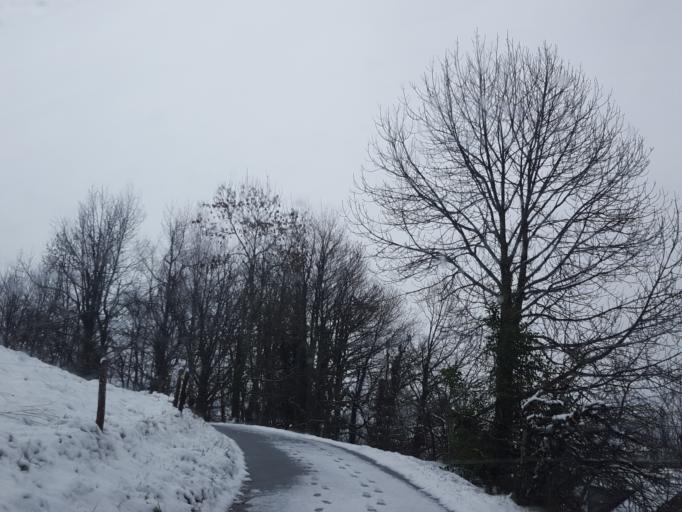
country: FR
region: Midi-Pyrenees
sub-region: Departement de l'Ariege
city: Montjoie-en-Couserans
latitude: 42.9037
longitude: 1.3556
